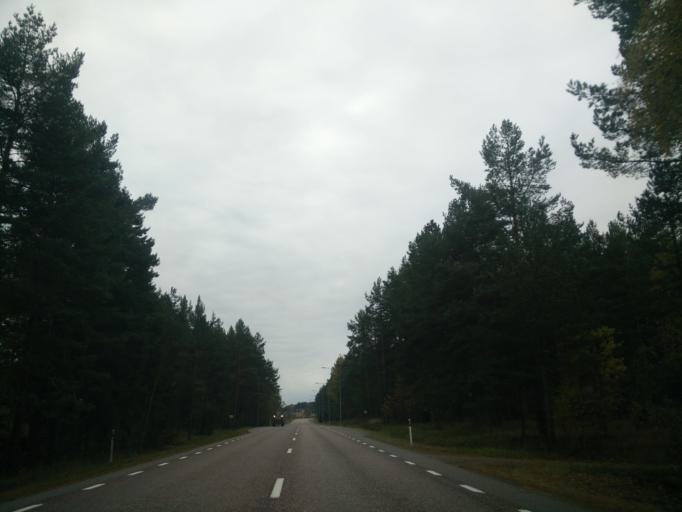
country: SE
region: Gaevleborg
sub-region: Gavle Kommun
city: Norrsundet
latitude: 60.8236
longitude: 17.2122
